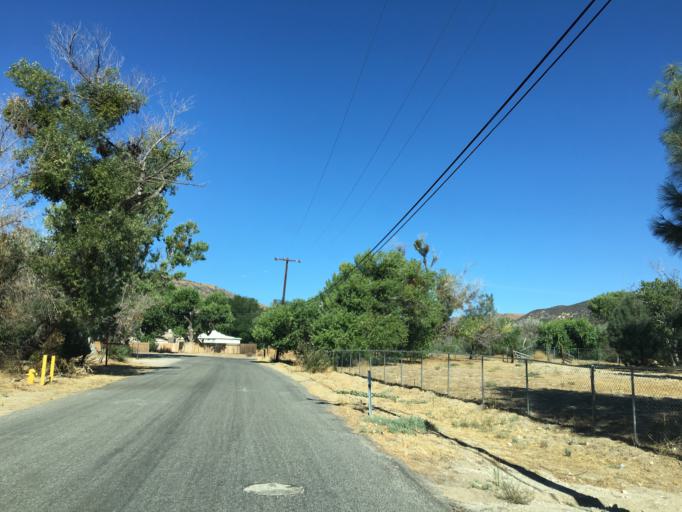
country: US
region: California
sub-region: Los Angeles County
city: Green Valley
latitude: 34.6772
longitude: -118.4517
